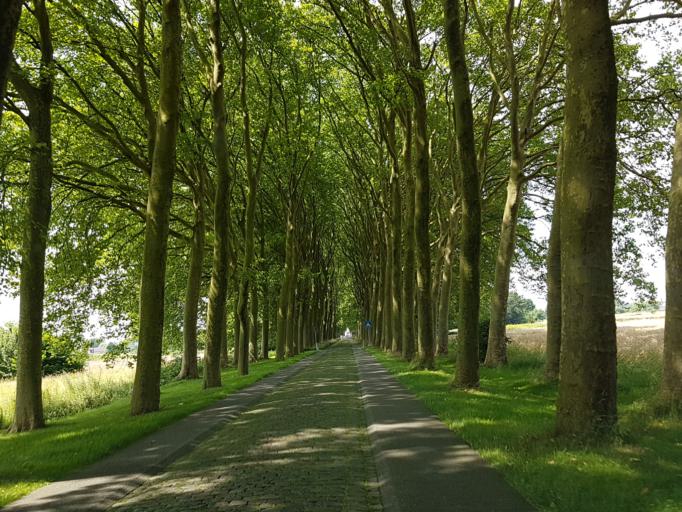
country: BE
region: Flanders
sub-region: Provincie Vlaams-Brabant
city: Kampenhout
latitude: 50.9378
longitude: 4.5752
